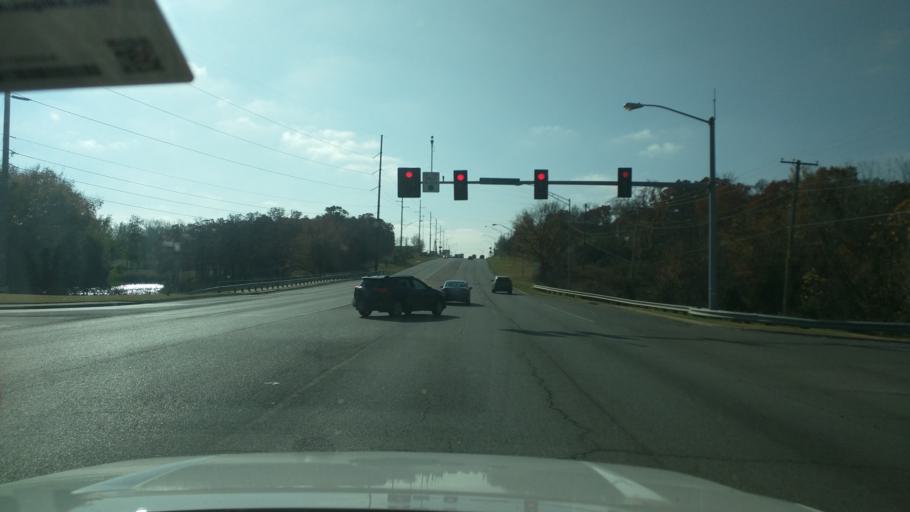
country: US
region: Oklahoma
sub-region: Washington County
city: Bartlesville
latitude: 36.7402
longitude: -95.9354
